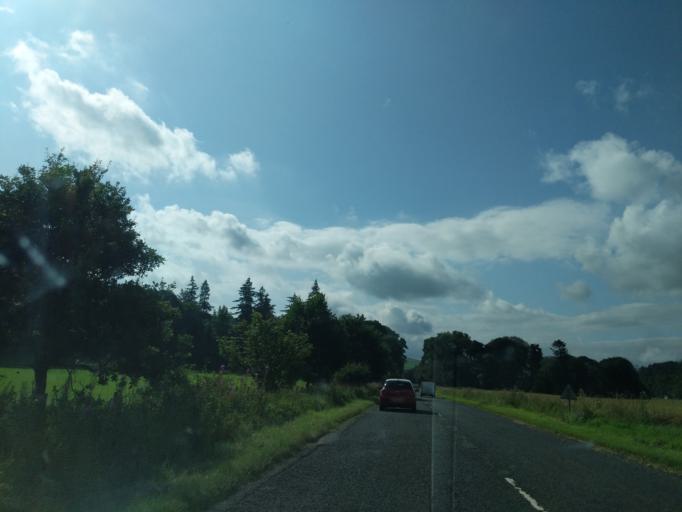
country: GB
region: Scotland
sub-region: The Scottish Borders
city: Peebles
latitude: 55.7268
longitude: -3.2054
